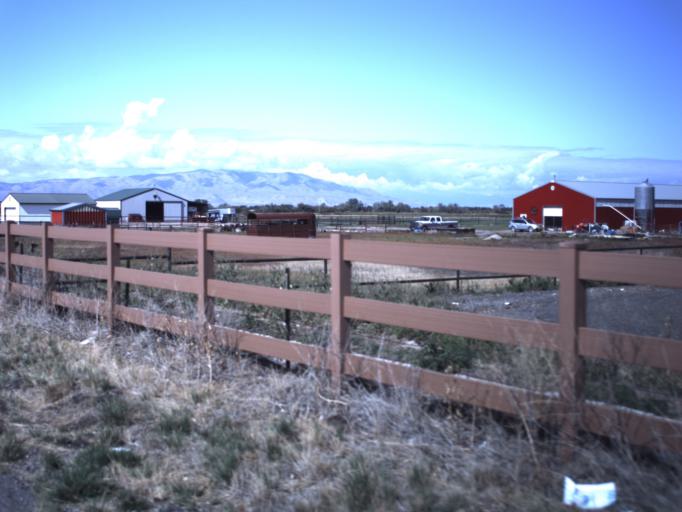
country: US
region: Utah
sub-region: Utah County
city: Spanish Fork
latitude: 40.1584
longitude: -111.7031
